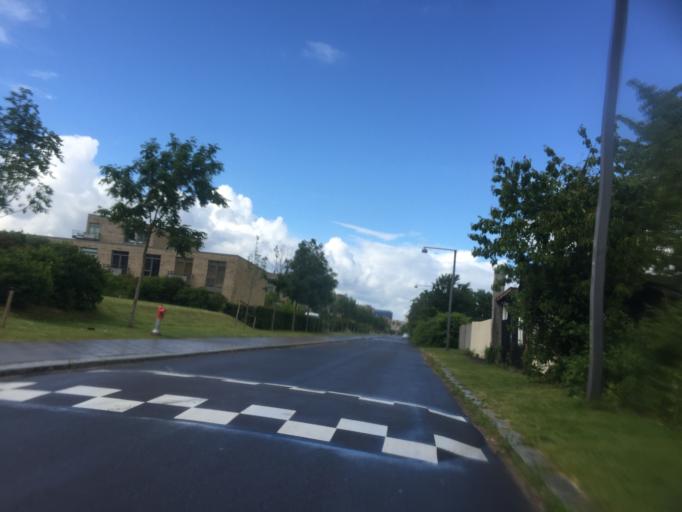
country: DK
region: Capital Region
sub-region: Tarnby Kommune
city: Tarnby
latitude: 55.6462
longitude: 12.5873
